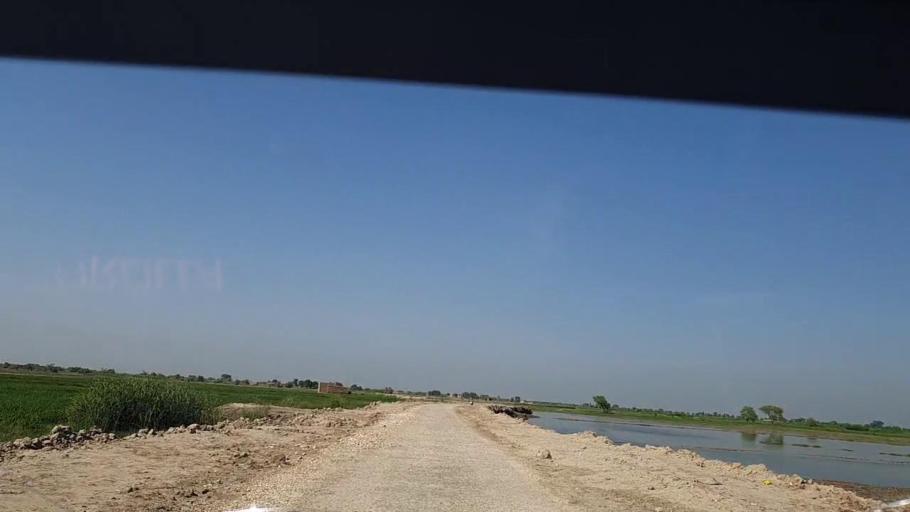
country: PK
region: Sindh
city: Tangwani
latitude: 28.3174
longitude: 69.0829
